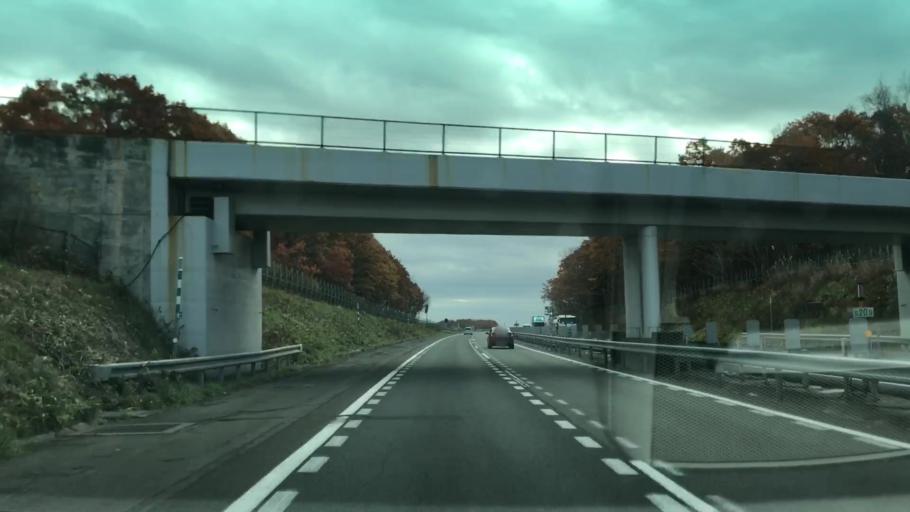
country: JP
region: Hokkaido
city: Kitahiroshima
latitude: 42.9188
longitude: 141.5458
